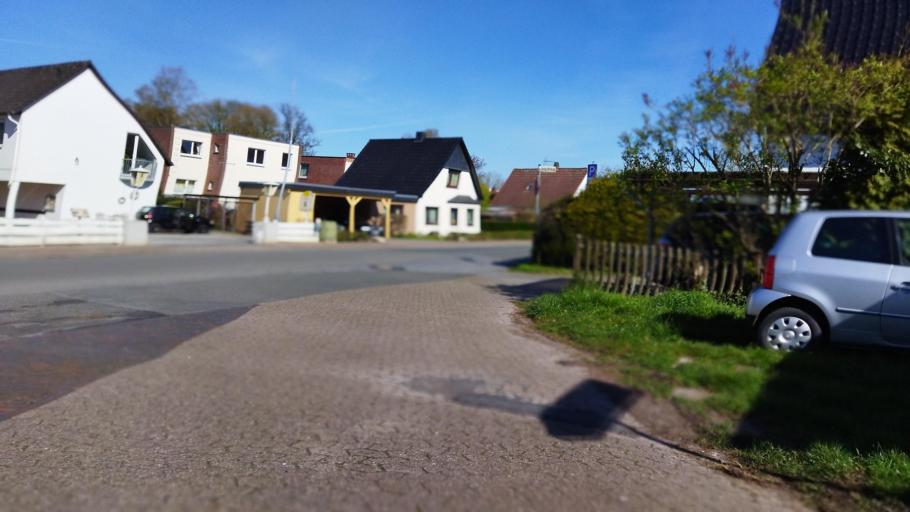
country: DE
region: Lower Saxony
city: Elsfleth
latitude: 53.2441
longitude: 8.4664
